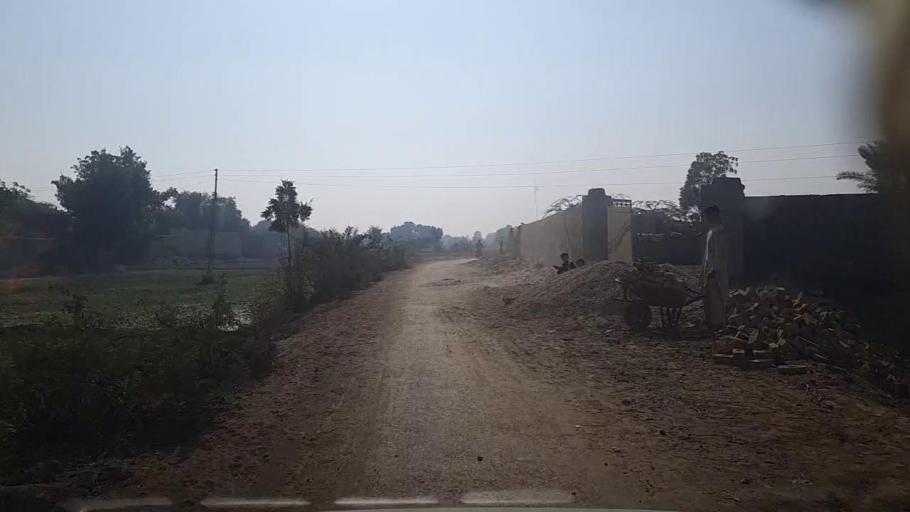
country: PK
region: Sindh
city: Kandiari
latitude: 27.0013
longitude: 68.4916
